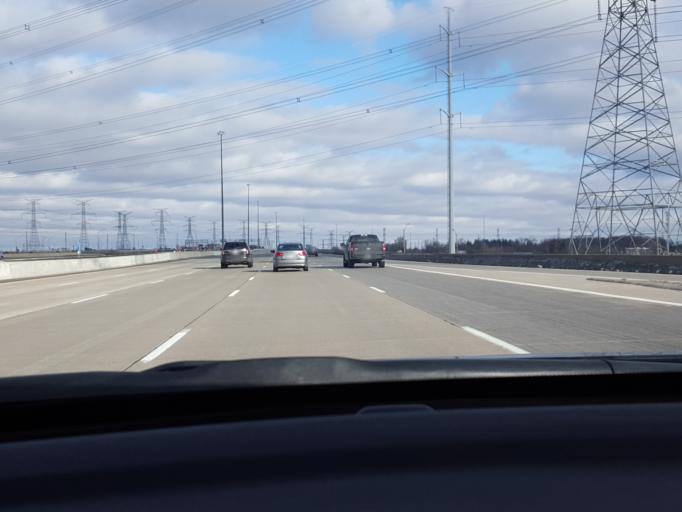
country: CA
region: Ontario
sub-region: York
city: Richmond Hill
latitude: 43.8334
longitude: -79.4304
